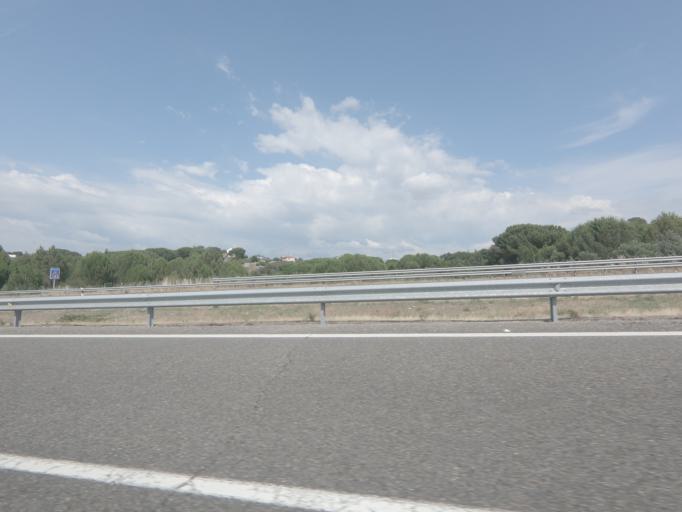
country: ES
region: Galicia
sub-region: Provincia de Ourense
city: Ourense
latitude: 42.3033
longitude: -7.8751
